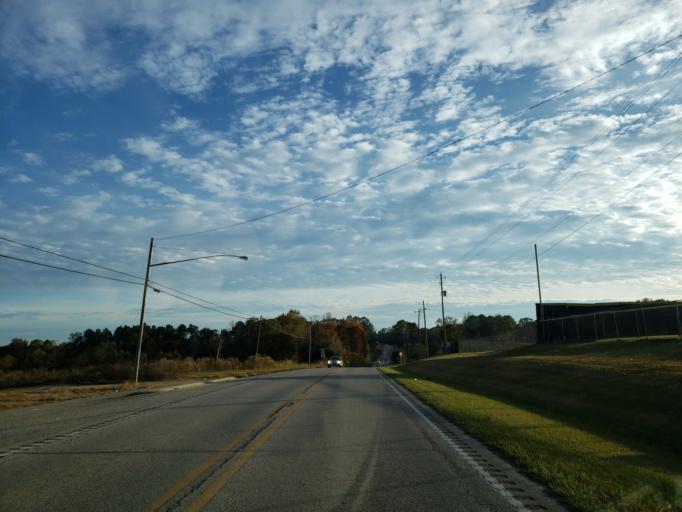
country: US
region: Mississippi
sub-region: Lamar County
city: Purvis
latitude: 31.1374
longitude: -89.4055
